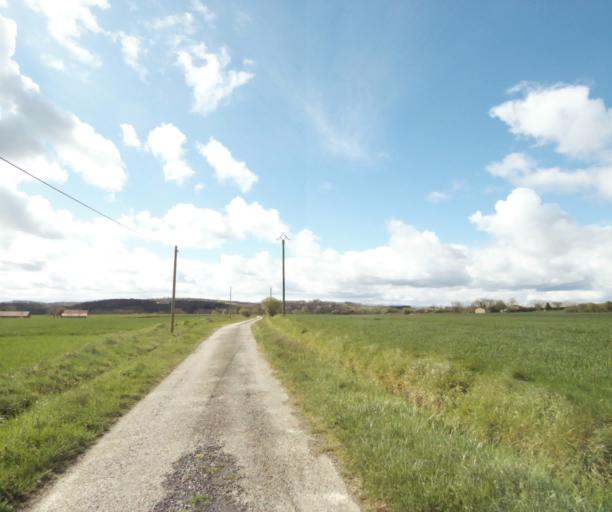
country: FR
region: Midi-Pyrenees
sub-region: Departement de l'Ariege
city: Saverdun
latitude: 43.2341
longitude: 1.5488
